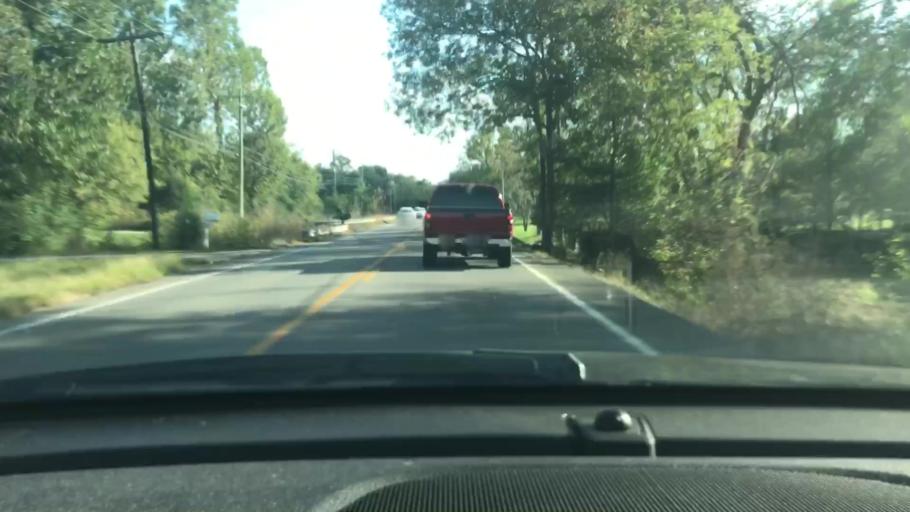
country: US
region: Tennessee
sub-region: Sumner County
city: Shackle Island
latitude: 36.3442
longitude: -86.6141
